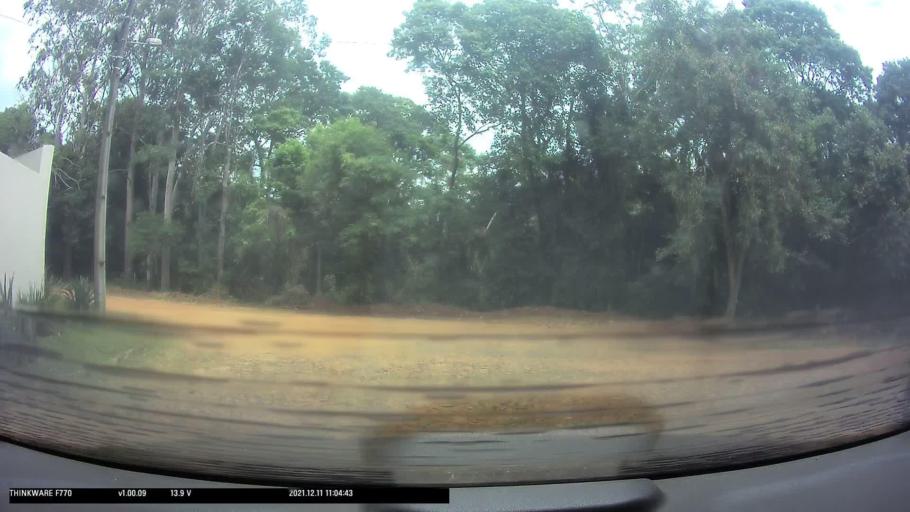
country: PY
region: Cordillera
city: Altos
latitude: -25.3018
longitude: -57.2415
